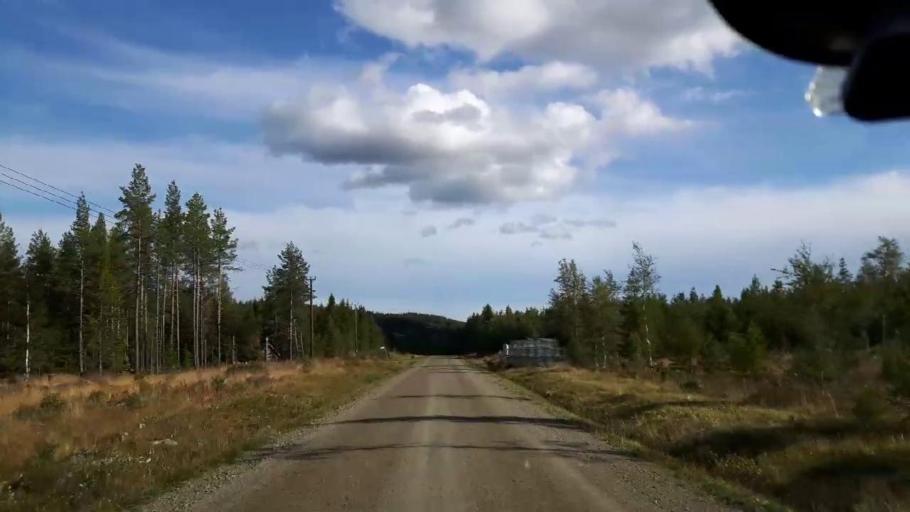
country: SE
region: Jaemtland
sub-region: Ragunda Kommun
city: Hammarstrand
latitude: 63.4263
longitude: 16.0561
